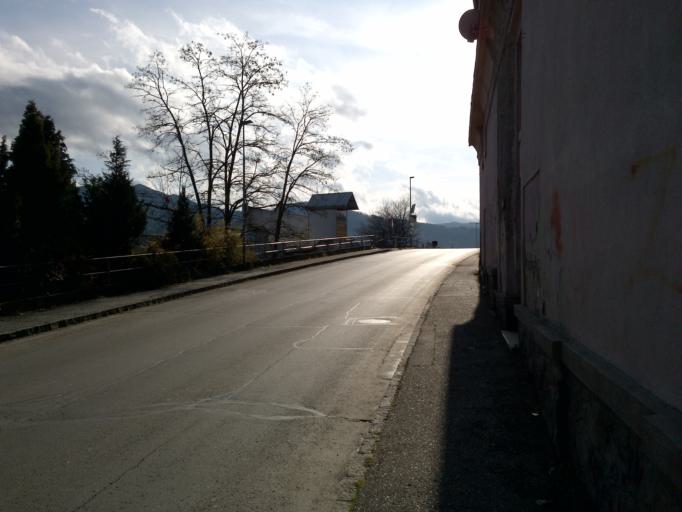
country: AT
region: Styria
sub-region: Politischer Bezirk Murtal
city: Apfelberg
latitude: 47.2139
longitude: 14.8312
